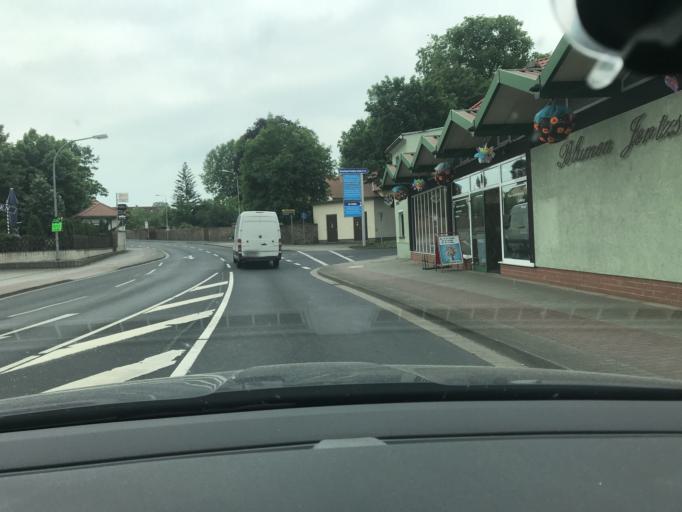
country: DE
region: Saxony
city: Grossenhain
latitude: 51.2866
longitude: 13.5311
